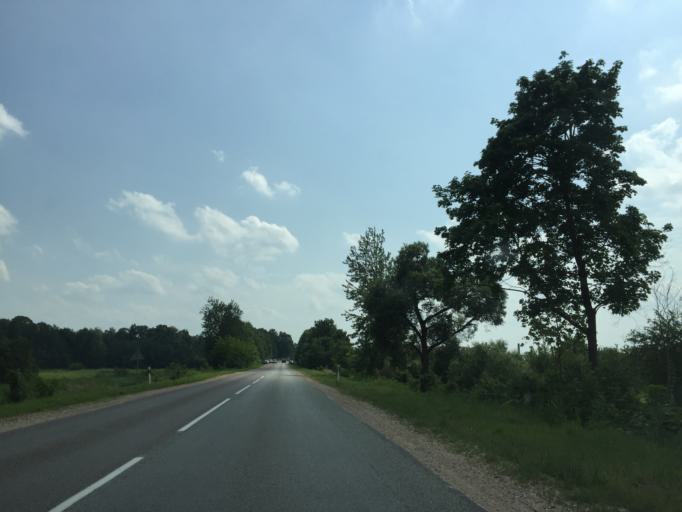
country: LV
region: Jelgava
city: Jelgava
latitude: 56.6919
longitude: 23.7189
